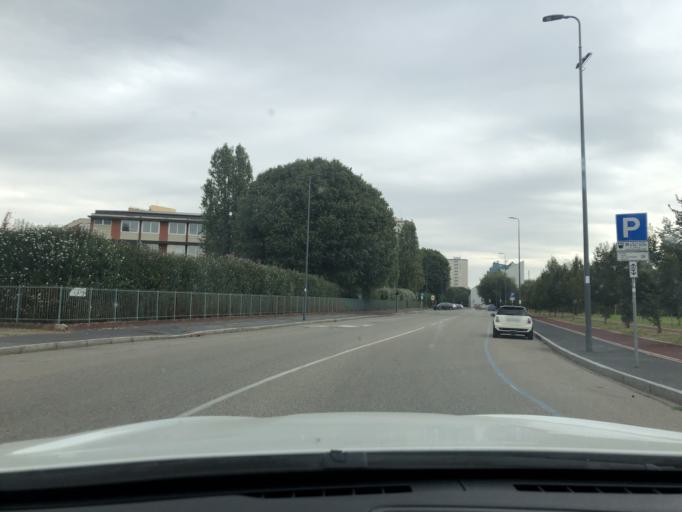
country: IT
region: Lombardy
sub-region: Citta metropolitana di Milano
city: Pero
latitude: 45.5041
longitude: 9.0979
